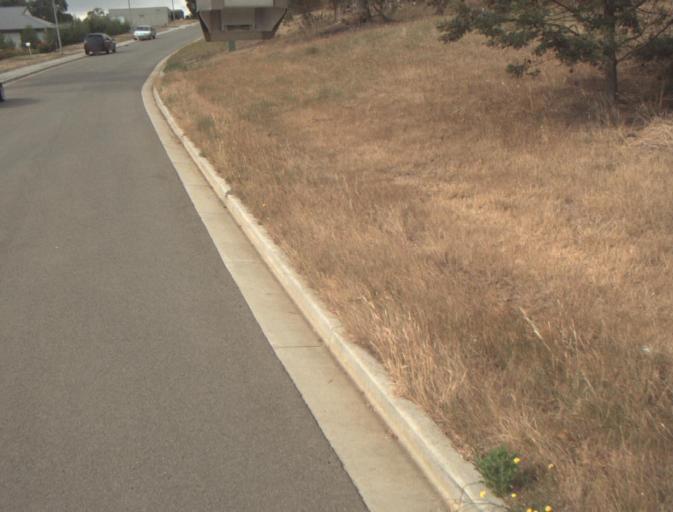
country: AU
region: Tasmania
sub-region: Launceston
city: Newstead
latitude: -41.4806
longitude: 147.1753
